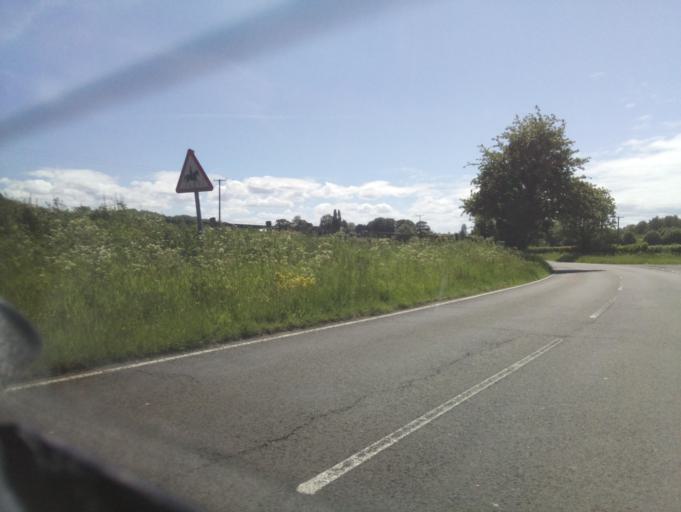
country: GB
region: Wales
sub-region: Monmouthshire
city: Caldicot
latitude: 51.6040
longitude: -2.7389
